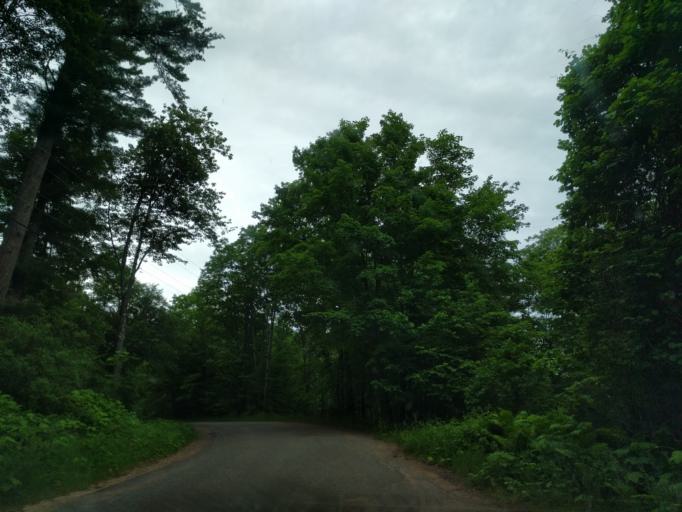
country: US
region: Michigan
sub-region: Marquette County
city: Trowbridge Park
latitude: 46.5728
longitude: -87.4768
